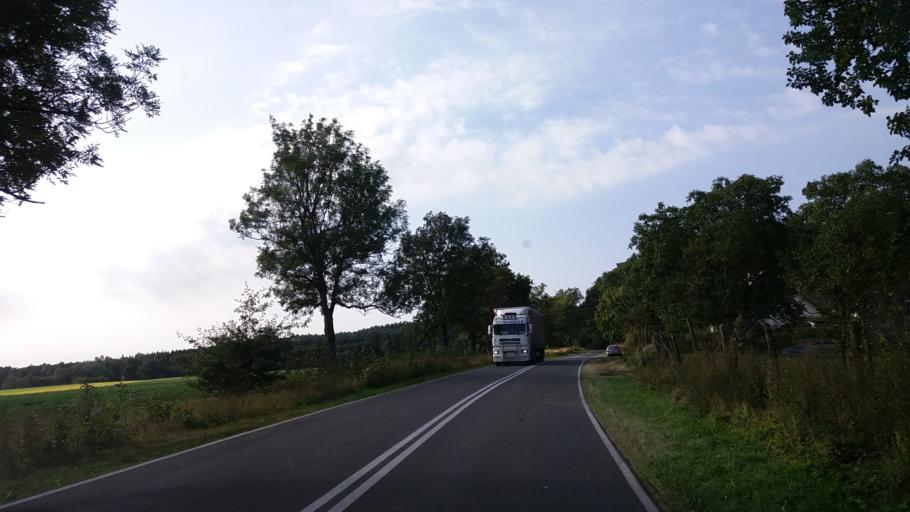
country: PL
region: West Pomeranian Voivodeship
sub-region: Powiat stargardzki
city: Suchan
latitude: 53.2450
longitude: 15.3249
